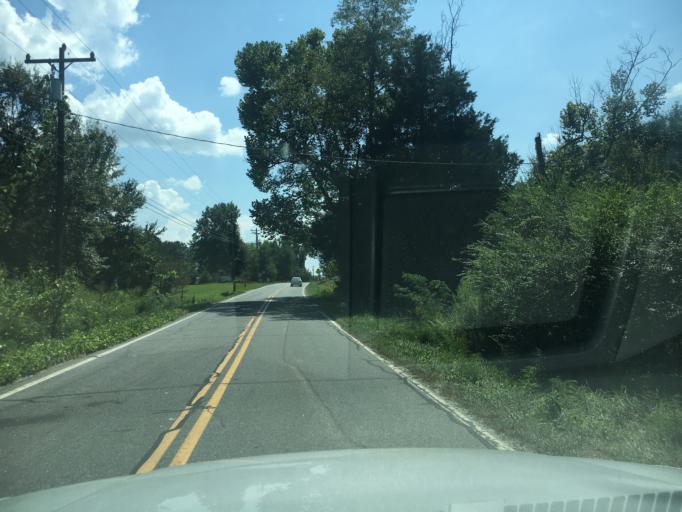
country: US
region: North Carolina
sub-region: Rutherford County
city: Forest City
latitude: 35.2751
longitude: -81.8431
